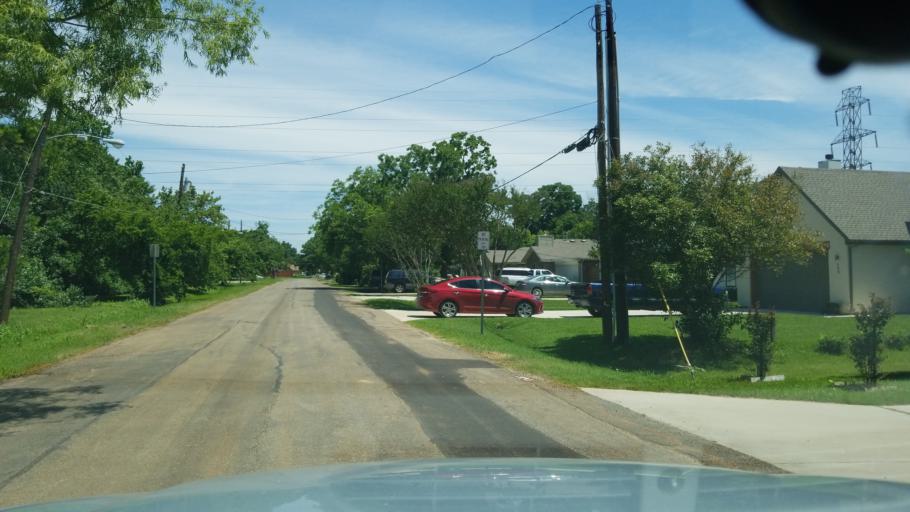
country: US
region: Texas
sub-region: Dallas County
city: Irving
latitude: 32.8154
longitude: -96.9321
